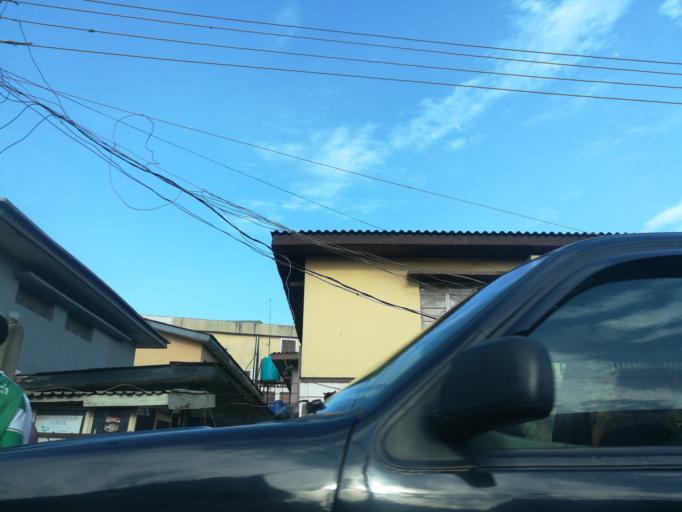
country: NG
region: Lagos
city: Ikeja
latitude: 6.5962
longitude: 3.3460
